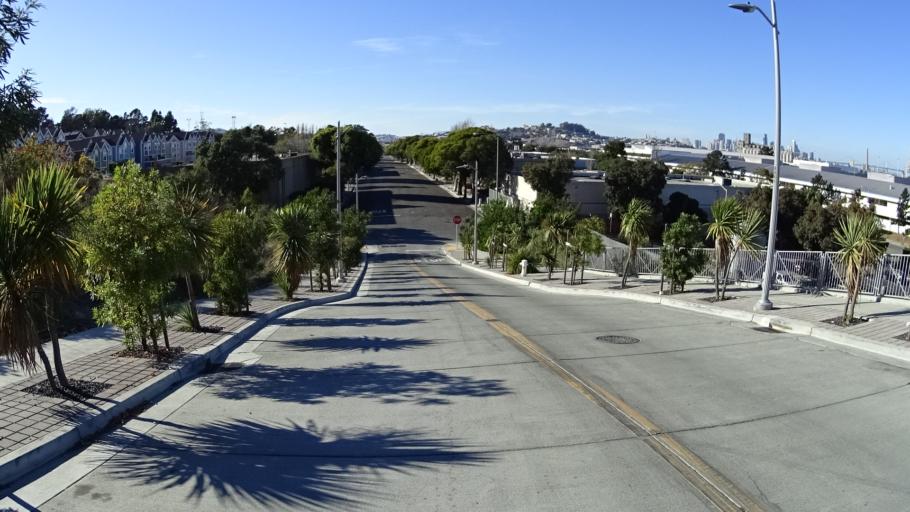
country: US
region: California
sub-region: San Francisco County
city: San Francisco
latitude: 37.7376
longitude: -122.3813
